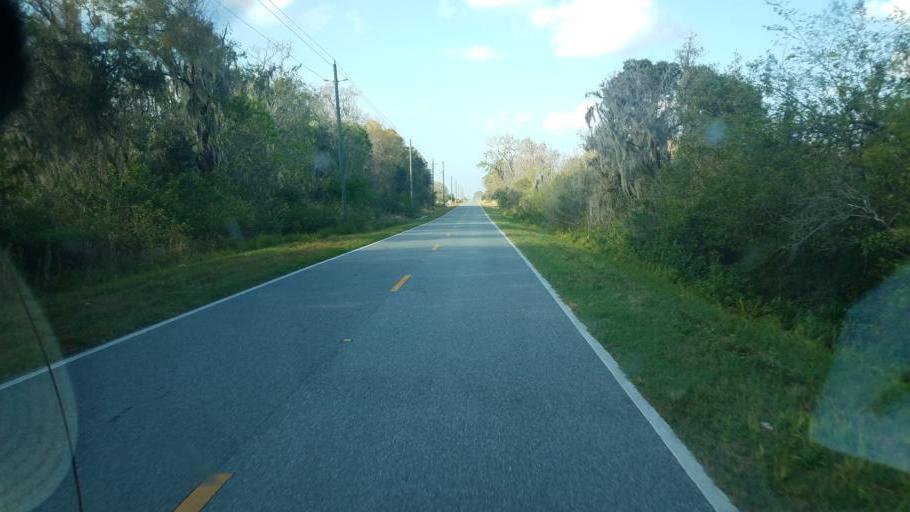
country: US
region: Florida
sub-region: Hardee County
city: Bowling Green
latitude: 27.6400
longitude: -81.9479
